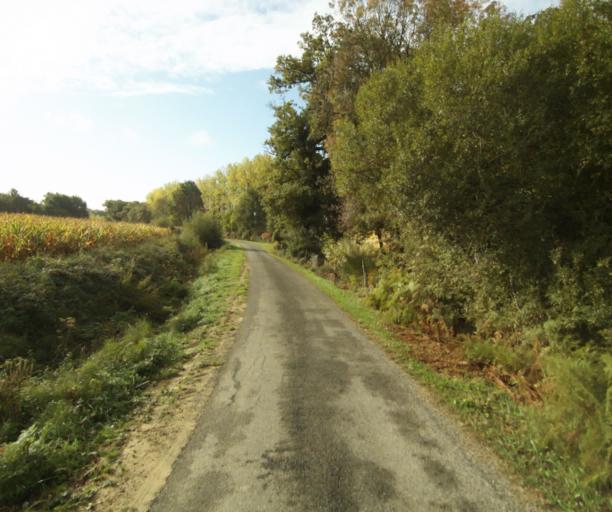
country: FR
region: Midi-Pyrenees
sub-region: Departement du Gers
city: Nogaro
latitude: 43.8040
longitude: -0.0678
